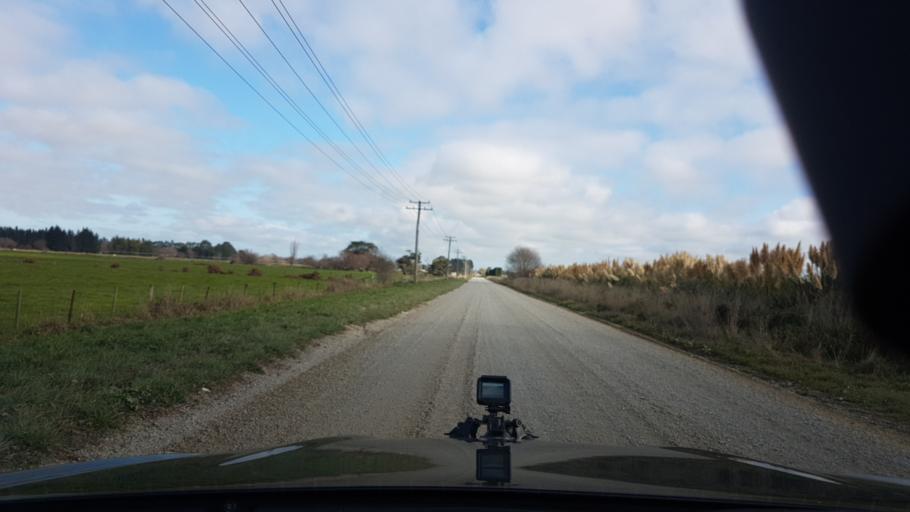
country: NZ
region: Canterbury
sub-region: Waimakariri District
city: Woodend
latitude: -43.3218
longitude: 172.6284
